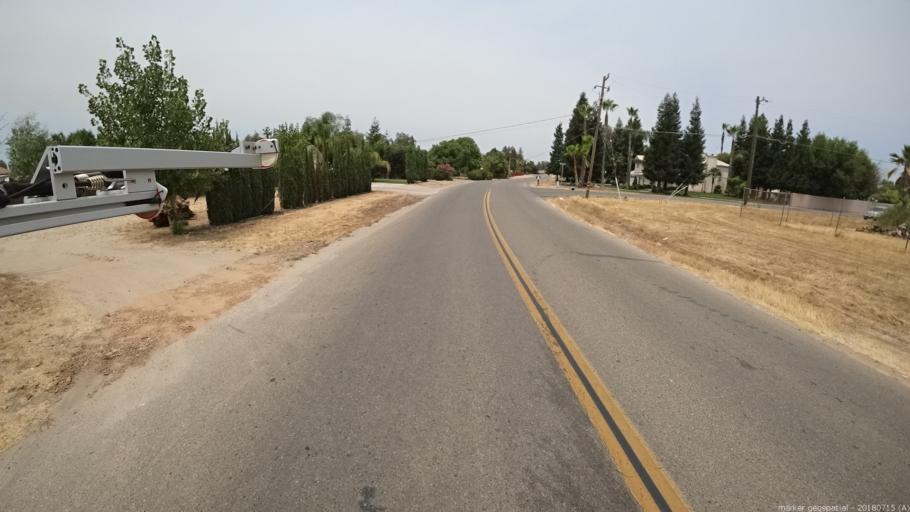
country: US
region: California
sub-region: Madera County
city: Madera Acres
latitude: 36.9980
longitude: -120.0874
